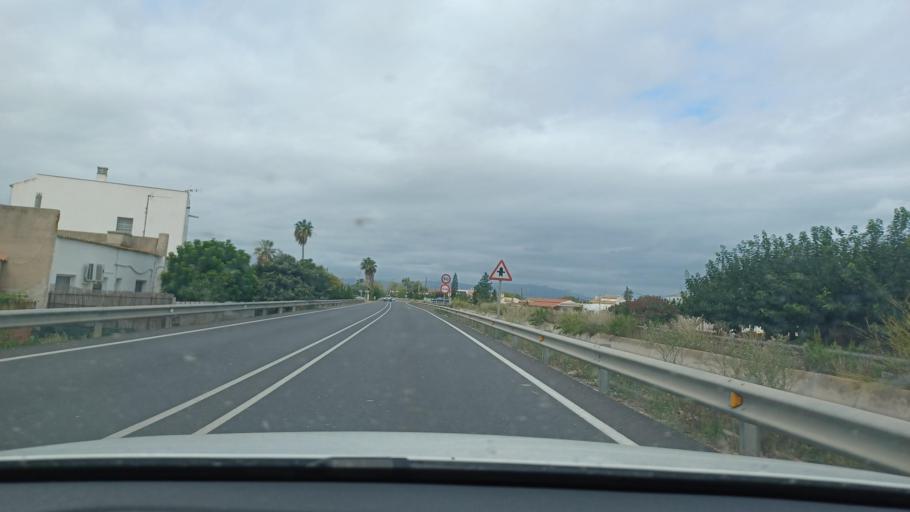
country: ES
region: Catalonia
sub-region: Provincia de Tarragona
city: Deltebre
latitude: 40.7170
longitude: 0.7508
